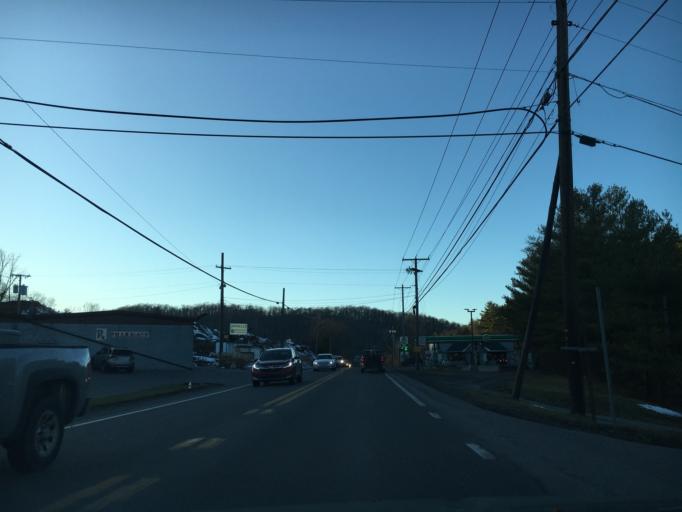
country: US
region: West Virginia
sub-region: Raleigh County
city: Shady Spring
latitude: 37.7281
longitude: -81.1049
